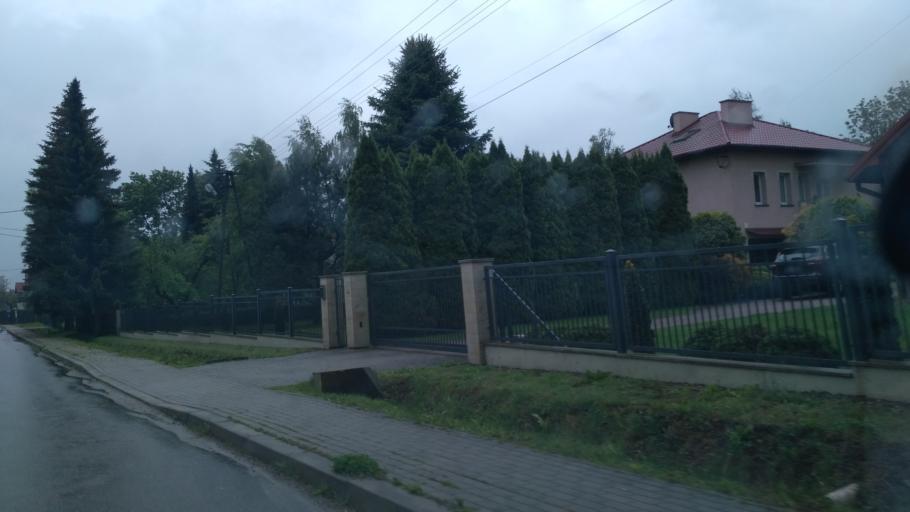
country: PL
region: Subcarpathian Voivodeship
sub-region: Powiat jasielski
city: Tarnowiec
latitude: 49.7658
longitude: 21.5409
